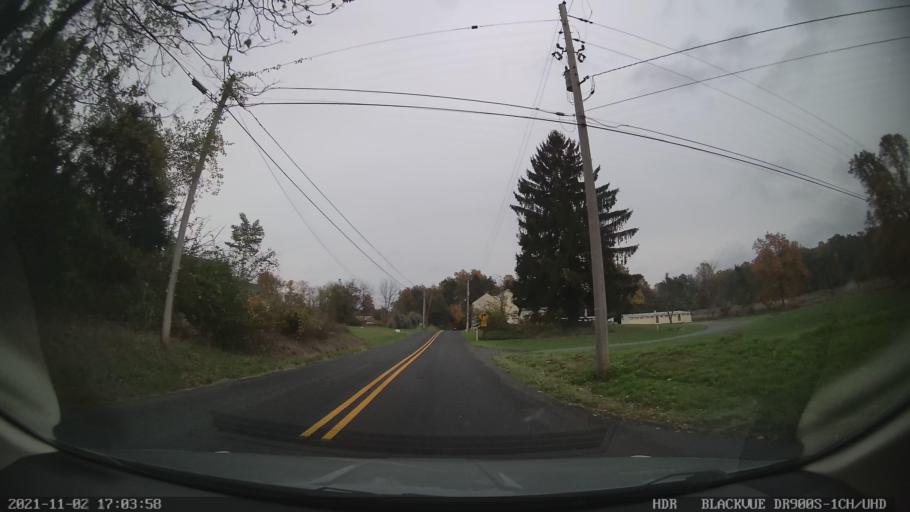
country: US
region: Pennsylvania
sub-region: Berks County
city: Fleetwood
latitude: 40.4405
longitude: -75.8400
